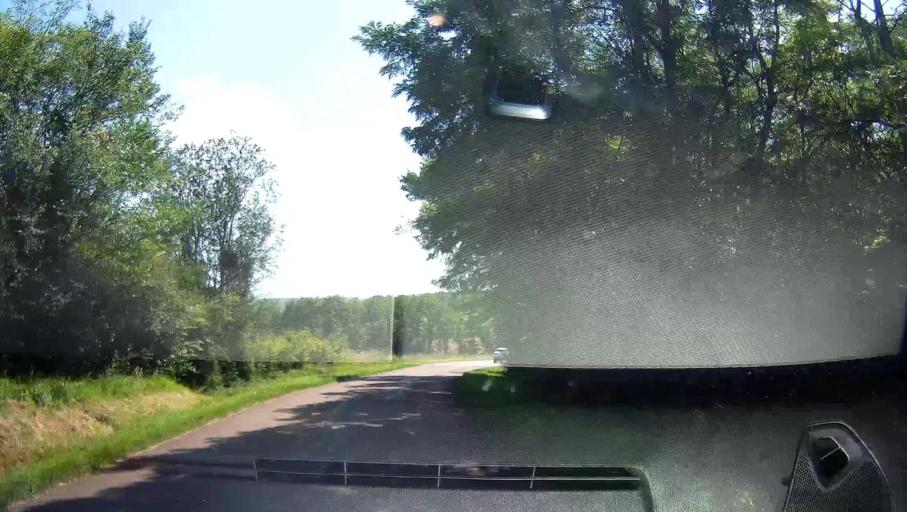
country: FR
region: Bourgogne
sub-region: Departement de Saone-et-Loire
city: Saint-Leger-sur-Dheune
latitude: 46.8779
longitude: 4.6368
